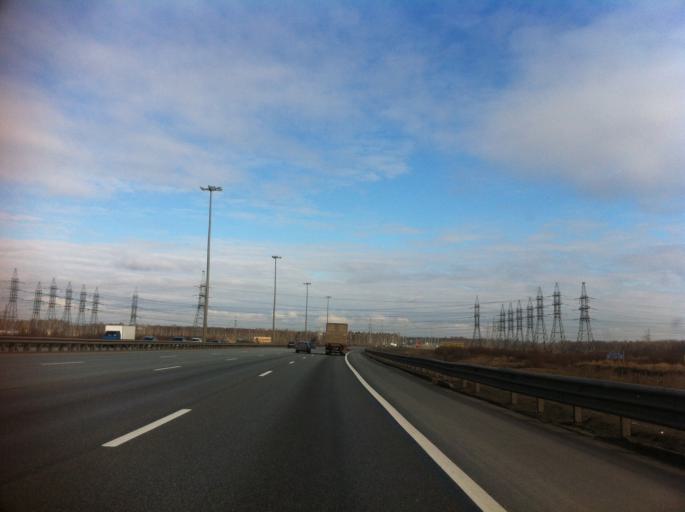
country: RU
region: St.-Petersburg
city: Krasnogvargeisky
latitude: 59.9208
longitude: 30.5271
